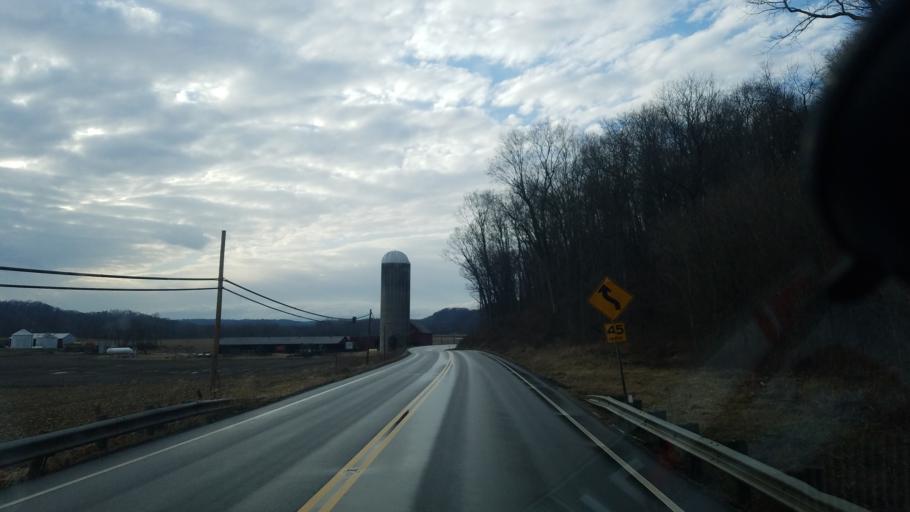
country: US
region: Ohio
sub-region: Coshocton County
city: Coshocton
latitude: 40.3407
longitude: -82.0231
